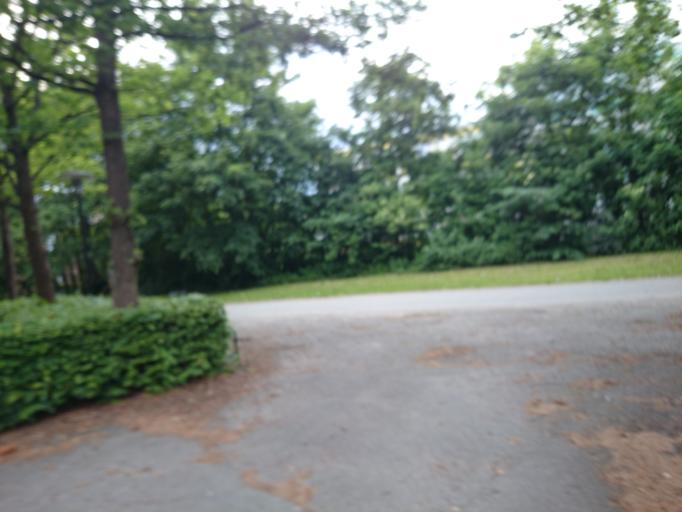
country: SE
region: Skane
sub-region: Lunds Kommun
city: Lund
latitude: 55.7076
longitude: 13.2148
